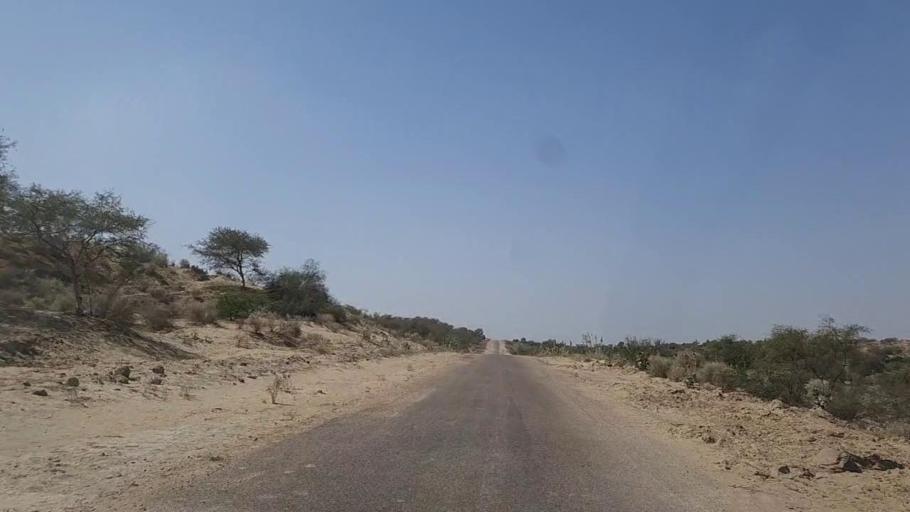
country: PK
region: Sindh
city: Diplo
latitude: 24.5521
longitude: 69.4317
